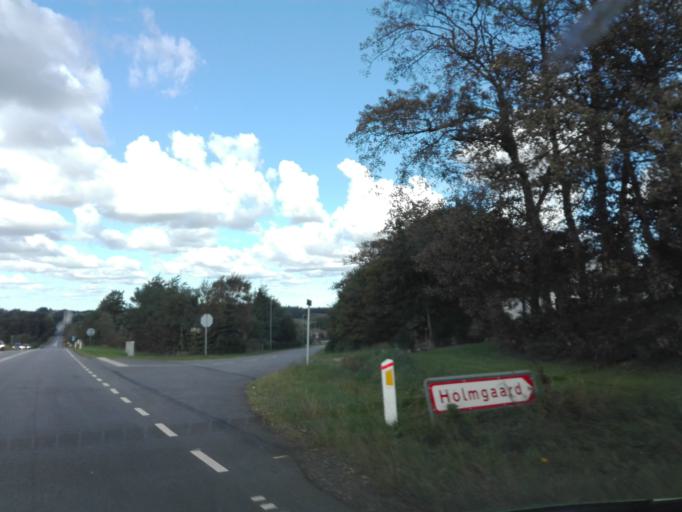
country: DK
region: North Denmark
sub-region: Mariagerfjord Kommune
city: Hobro
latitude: 56.5849
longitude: 9.8089
